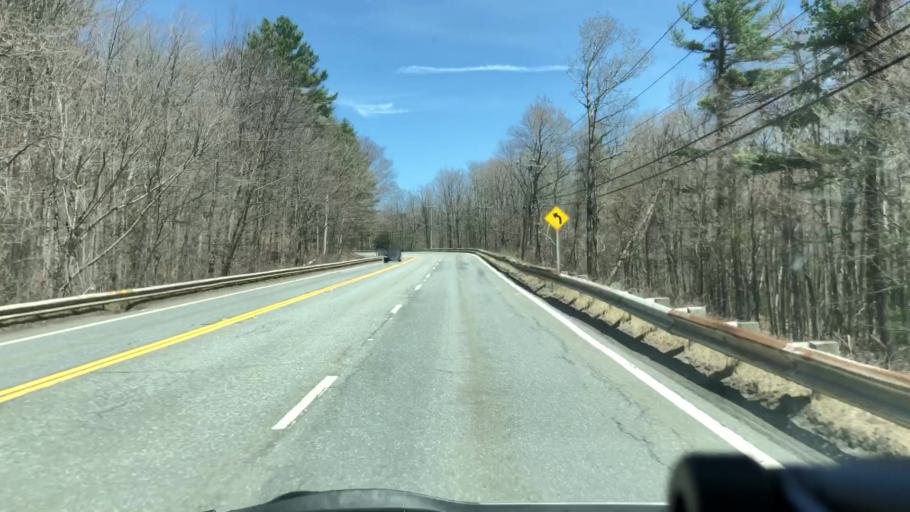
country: US
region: Massachusetts
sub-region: Berkshire County
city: Hinsdale
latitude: 42.4956
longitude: -73.1066
